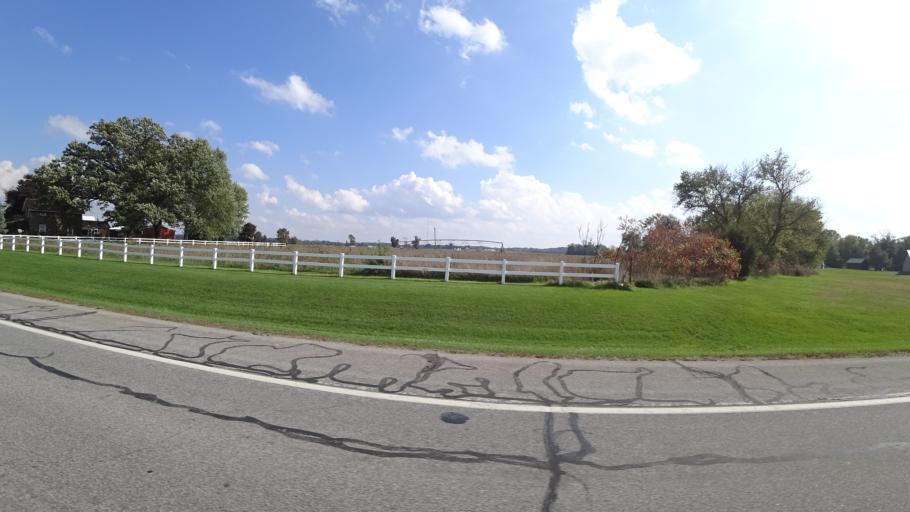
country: US
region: Michigan
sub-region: Saint Joseph County
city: Colon
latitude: 42.0275
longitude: -85.3469
